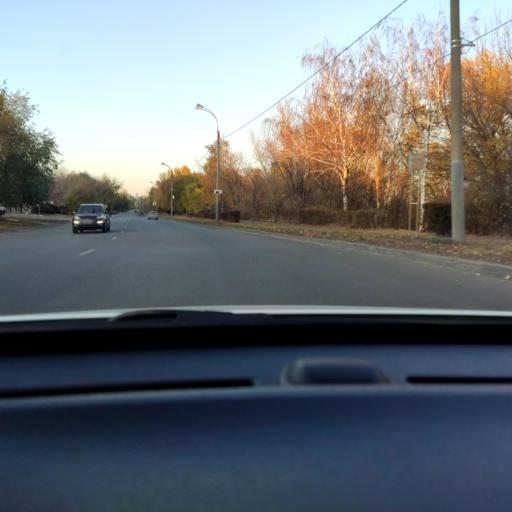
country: RU
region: Voronezj
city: Voronezh
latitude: 51.6398
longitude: 39.2107
